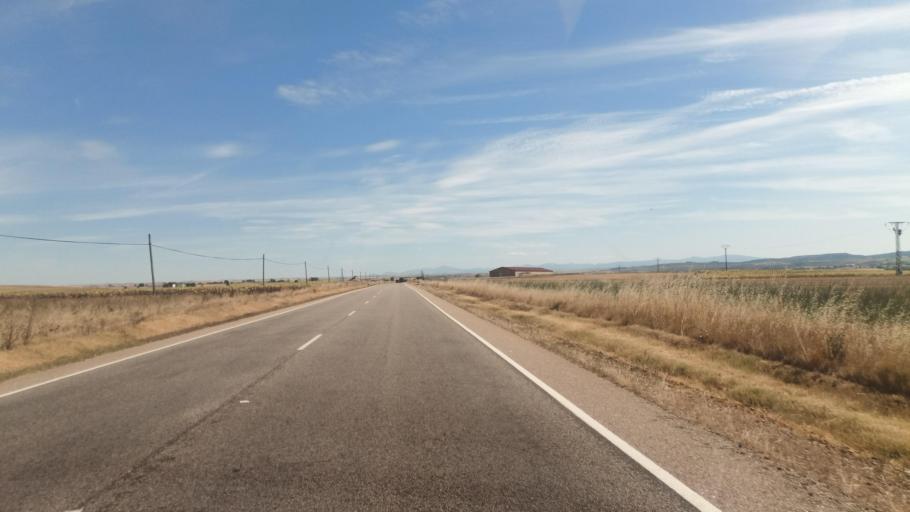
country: ES
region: Castille and Leon
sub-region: Provincia de Burgos
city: Quintanabureba
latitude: 42.6342
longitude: -3.3812
